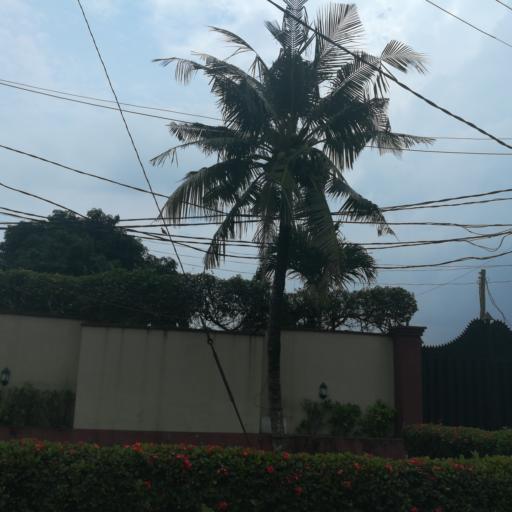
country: NG
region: Lagos
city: Ojota
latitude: 6.5761
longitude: 3.3806
